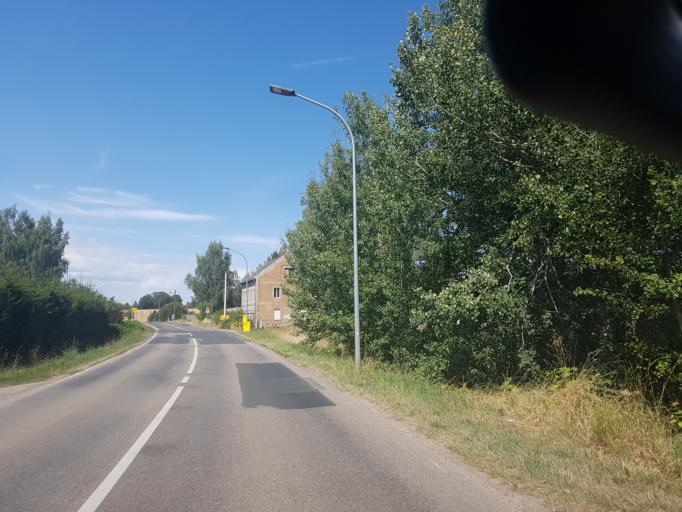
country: DE
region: Saxony
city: Hartha
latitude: 51.0832
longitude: 12.9913
